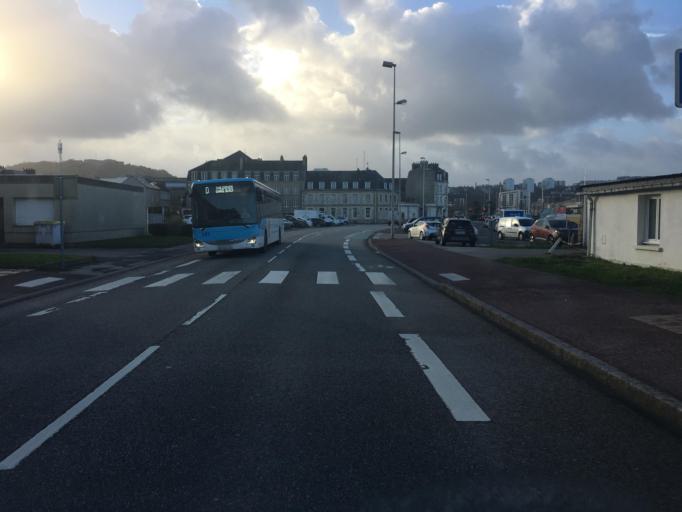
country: FR
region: Lower Normandy
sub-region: Departement de la Manche
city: Cherbourg-Octeville
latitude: 49.6410
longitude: -1.6181
